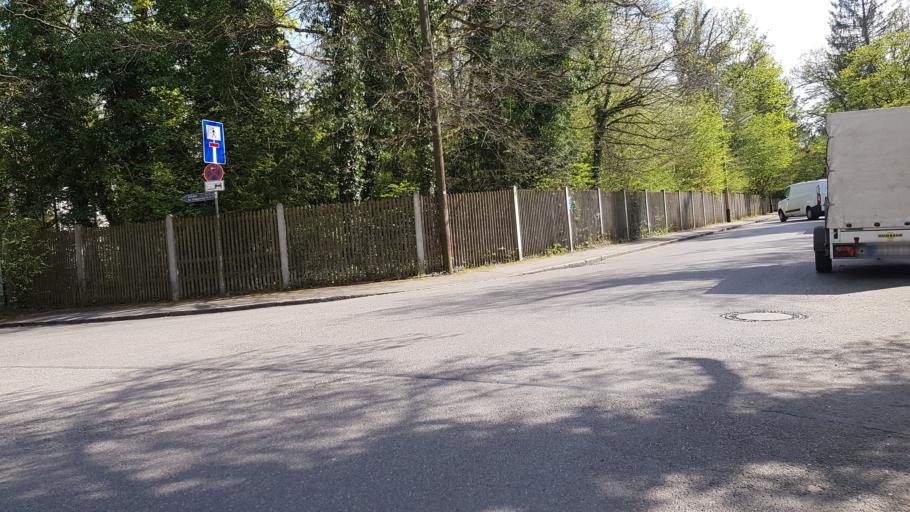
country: DE
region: Bavaria
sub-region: Upper Bavaria
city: Pasing
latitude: 48.1725
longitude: 11.4883
